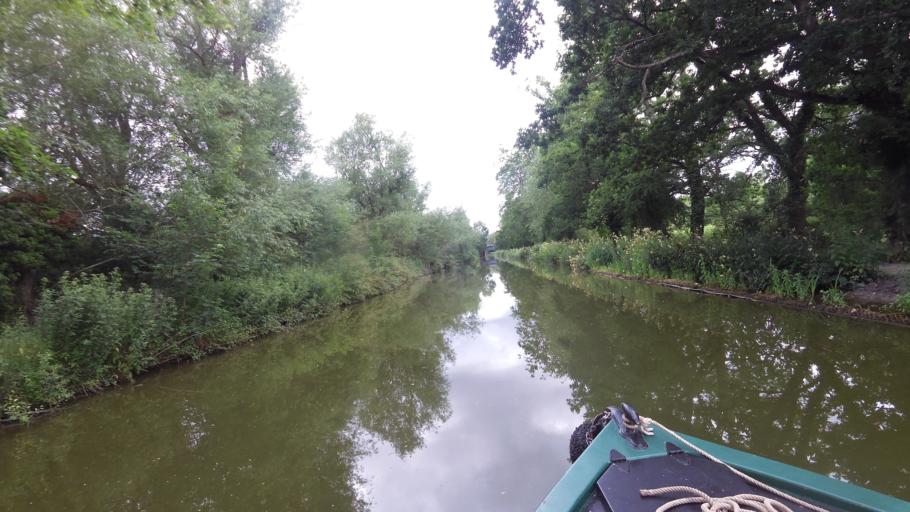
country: GB
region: England
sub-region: West Berkshire
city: Kintbury
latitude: 51.4072
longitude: -1.4708
